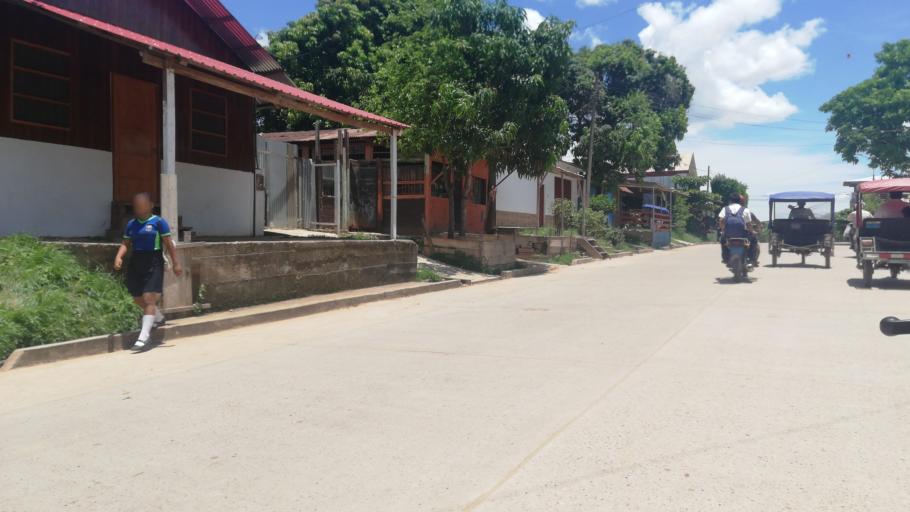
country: PE
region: Ucayali
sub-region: Provincia de Coronel Portillo
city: Puerto Callao
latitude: -8.3572
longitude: -74.5771
